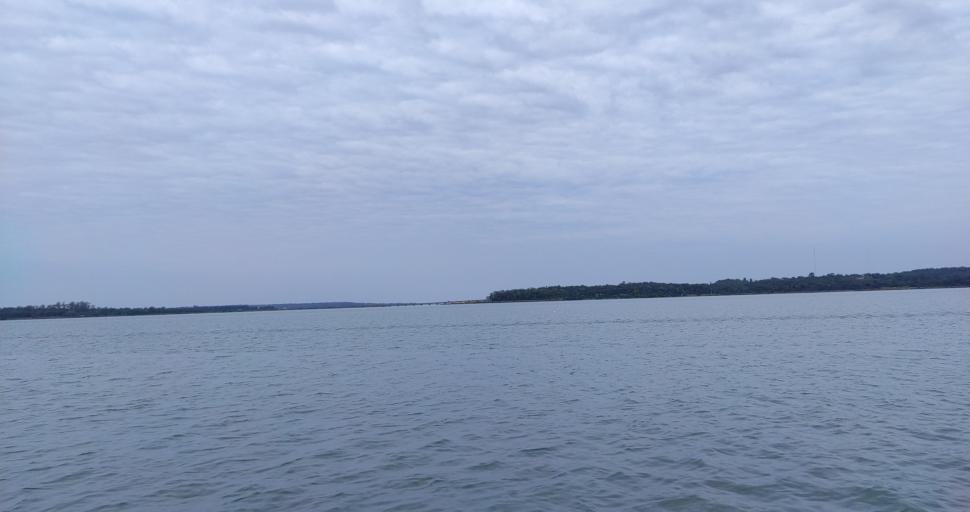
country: AR
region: Misiones
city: Garupa
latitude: -27.4414
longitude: -55.8111
